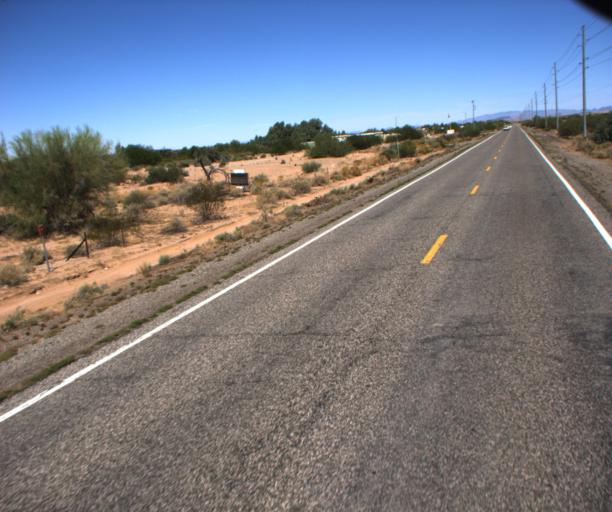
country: US
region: Arizona
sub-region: La Paz County
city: Cienega Springs
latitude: 33.9459
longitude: -114.0161
